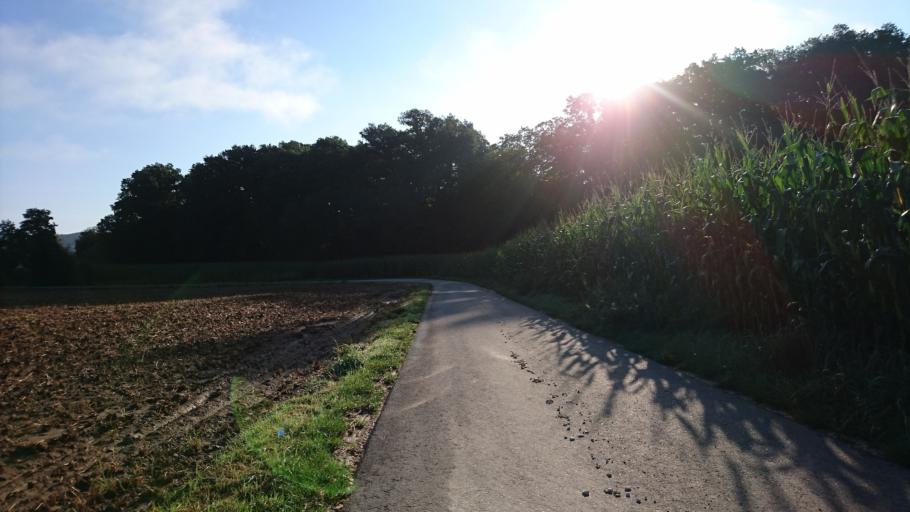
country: DE
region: Bavaria
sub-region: Swabia
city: Altenmunster
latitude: 48.4396
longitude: 10.5854
